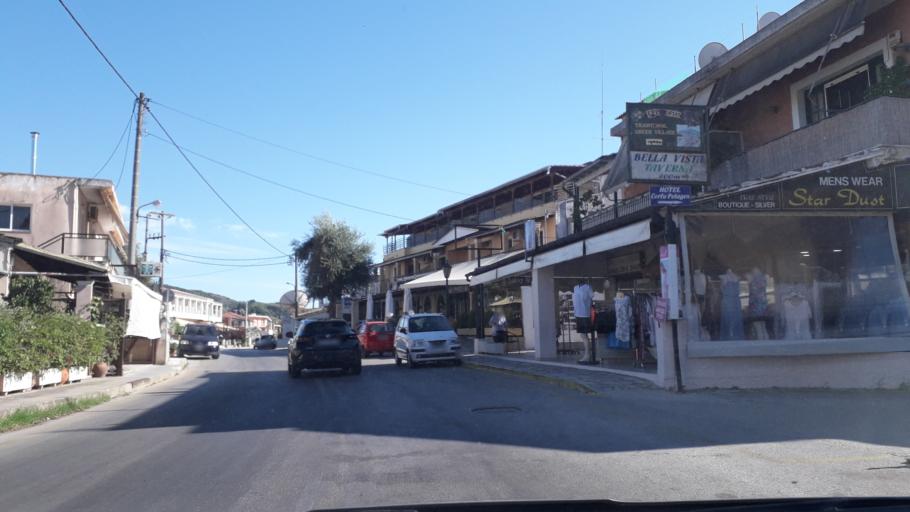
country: GR
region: Ionian Islands
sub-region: Nomos Kerkyras
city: Agios Matthaios
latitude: 39.4855
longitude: 19.9249
